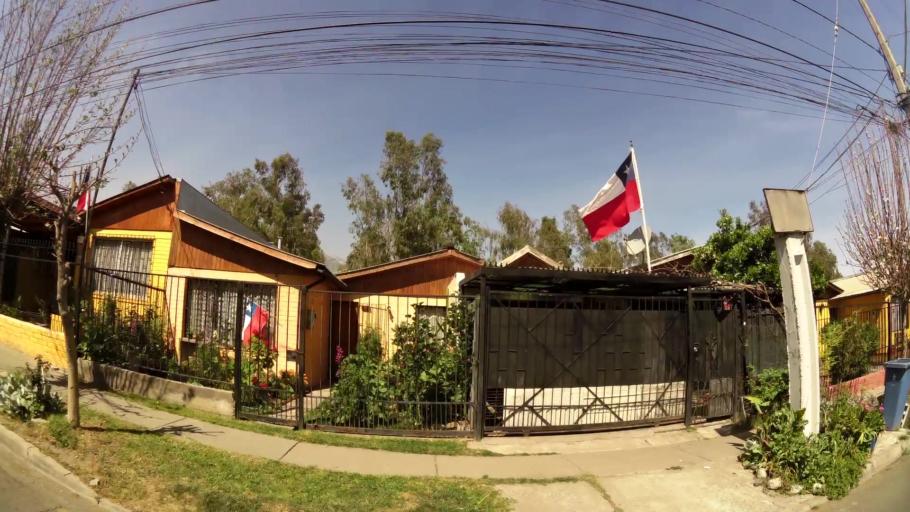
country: CL
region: Santiago Metropolitan
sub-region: Provincia de Santiago
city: Villa Presidente Frei, Nunoa, Santiago, Chile
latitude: -33.5285
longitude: -70.5624
